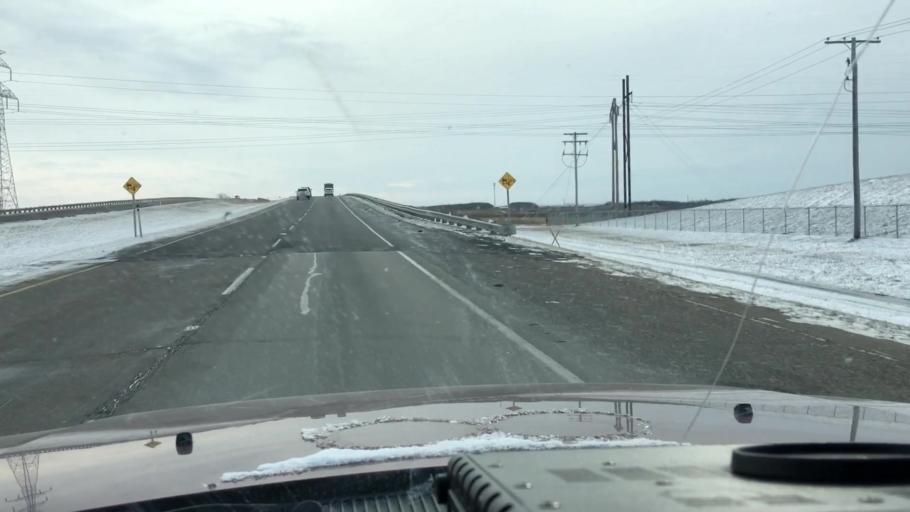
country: CA
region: Saskatchewan
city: Saskatoon
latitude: 52.0725
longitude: -106.6043
